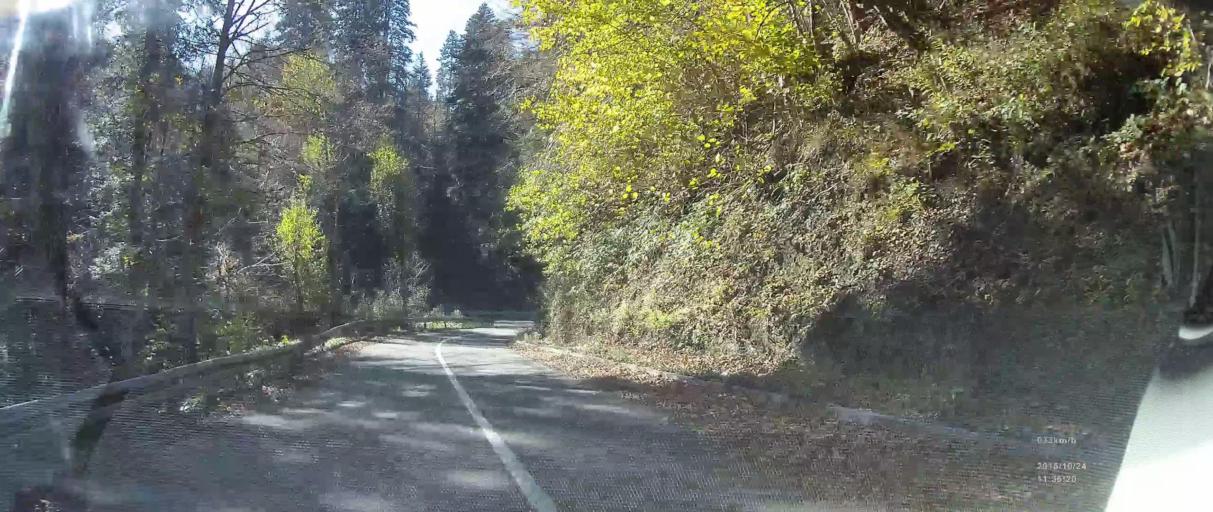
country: HR
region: Primorsko-Goranska
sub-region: Grad Delnice
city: Delnice
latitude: 45.3959
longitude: 14.7006
